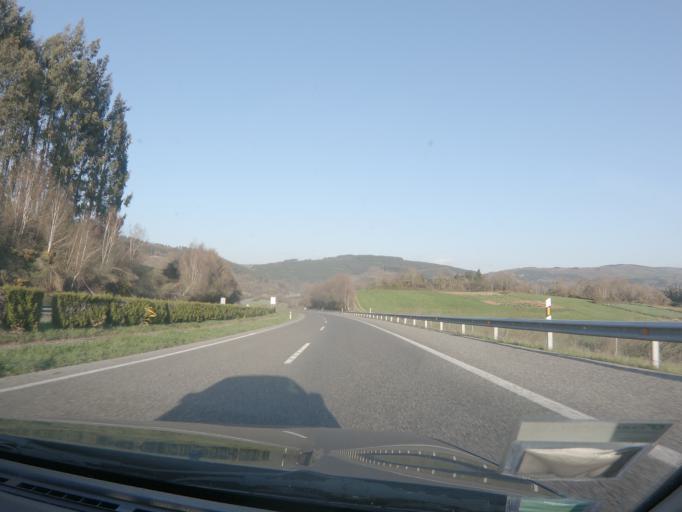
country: ES
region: Galicia
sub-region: Provincia de Lugo
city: Baralla
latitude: 42.9003
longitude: -7.2621
